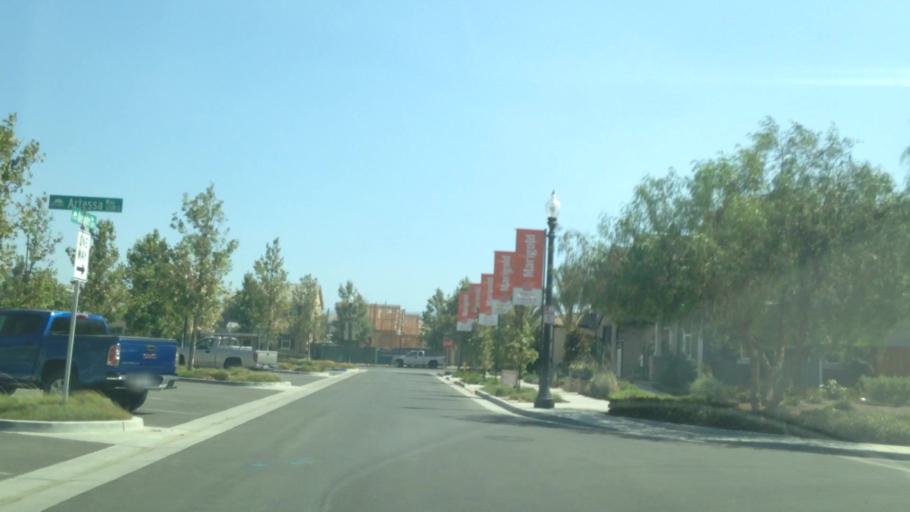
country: US
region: California
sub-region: Riverside County
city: Mira Loma
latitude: 34.0018
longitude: -117.5813
